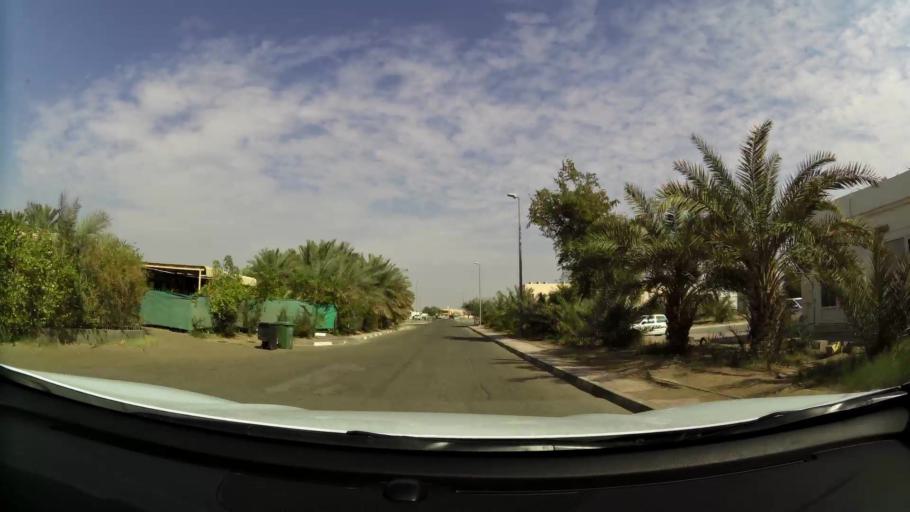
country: AE
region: Abu Dhabi
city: Al Ain
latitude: 24.0948
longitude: 55.9173
